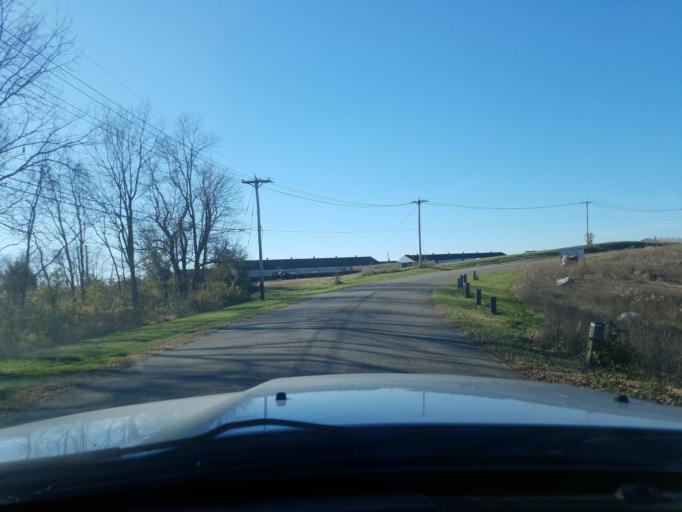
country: US
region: Indiana
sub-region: Clark County
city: Oak Park
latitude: 38.3630
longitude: -85.6865
